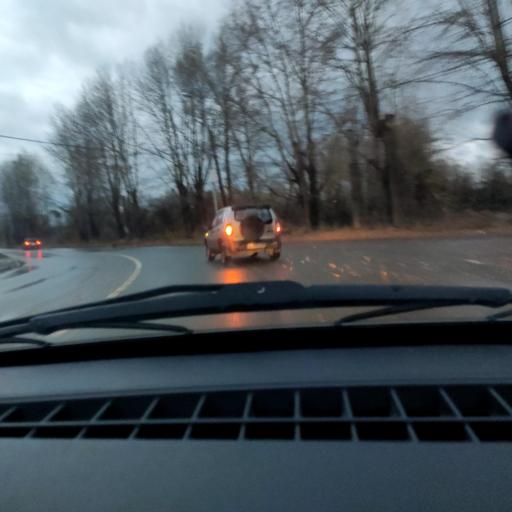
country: RU
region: Bashkortostan
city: Ufa
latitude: 54.8081
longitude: 56.0777
